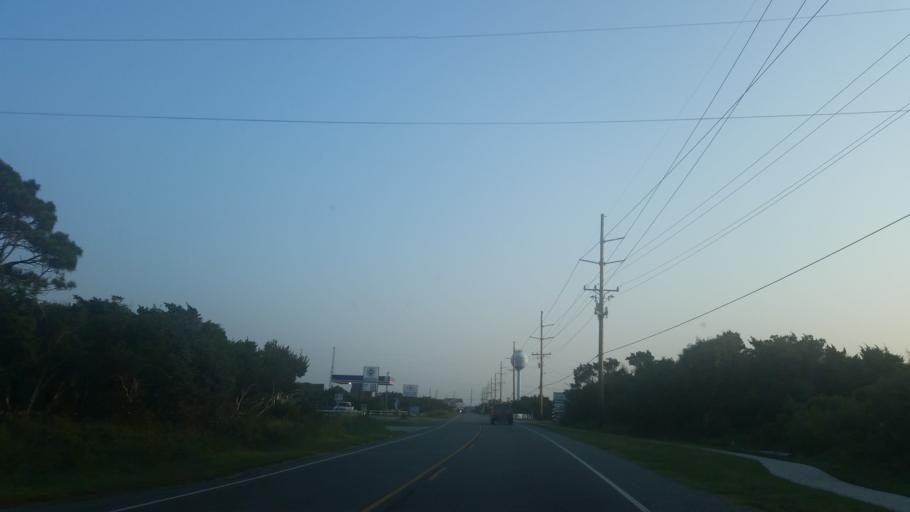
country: US
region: North Carolina
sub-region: Dare County
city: Wanchese
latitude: 35.5950
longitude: -75.4678
